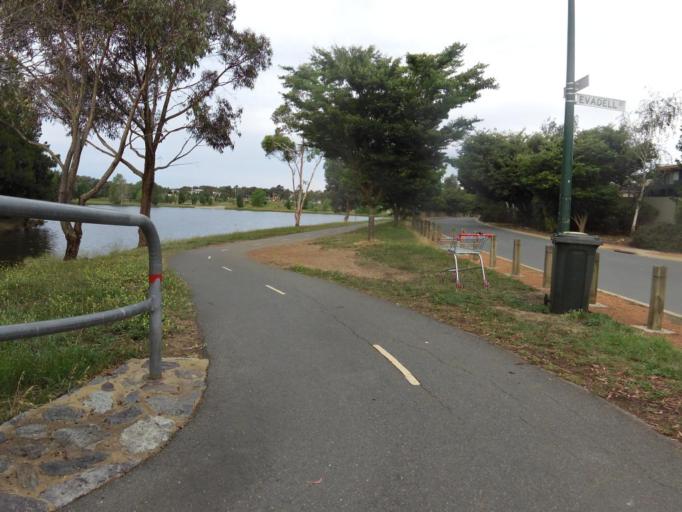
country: AU
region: Australian Capital Territory
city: Kaleen
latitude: -35.1751
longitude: 149.1361
